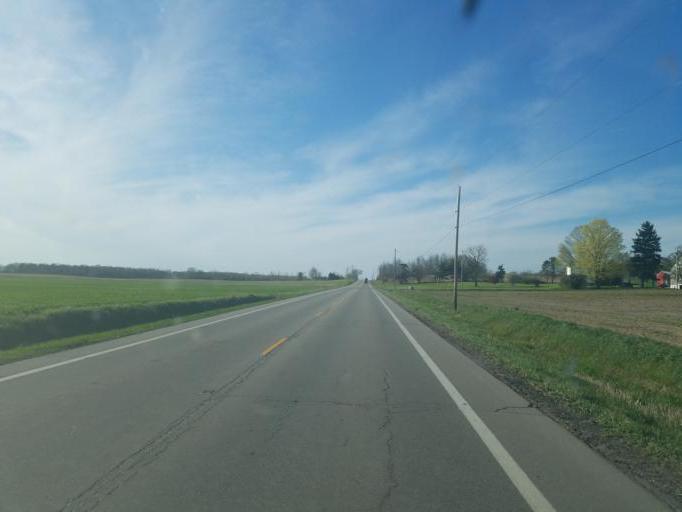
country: US
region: Ohio
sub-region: Ashland County
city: Ashland
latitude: 40.9259
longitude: -82.3481
